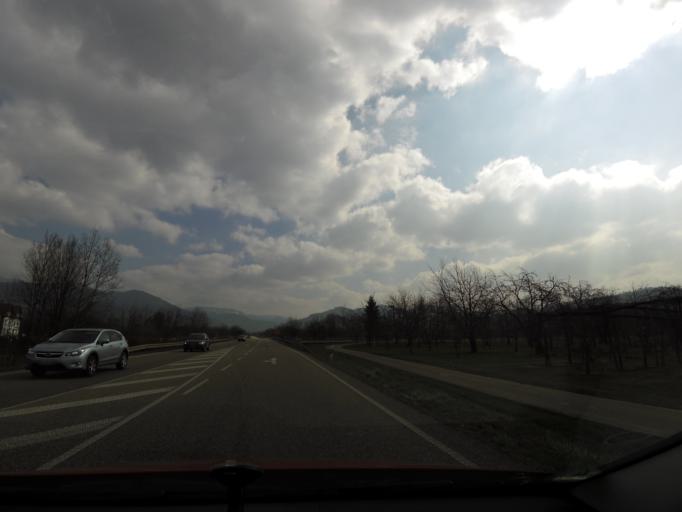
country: DE
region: Baden-Wuerttemberg
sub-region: Freiburg Region
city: Kappelrodeck
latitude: 48.6024
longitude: 8.0896
